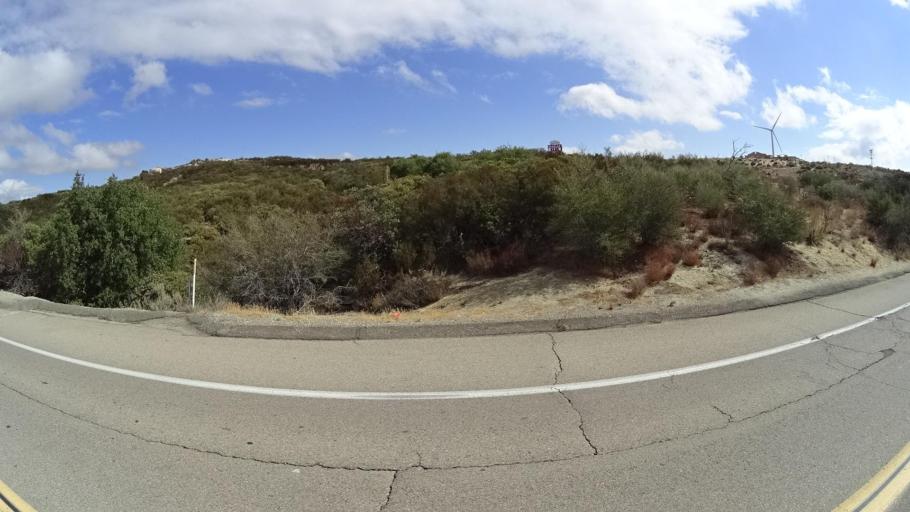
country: US
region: California
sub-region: San Diego County
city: Campo
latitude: 32.7030
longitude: -116.3595
